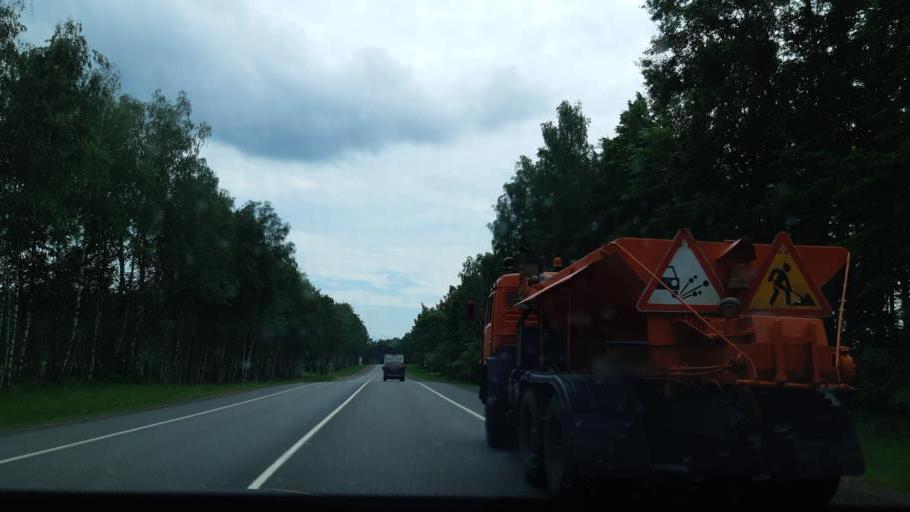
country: RU
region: Moskovskaya
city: Dorokhovo
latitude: 55.5002
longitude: 36.3472
